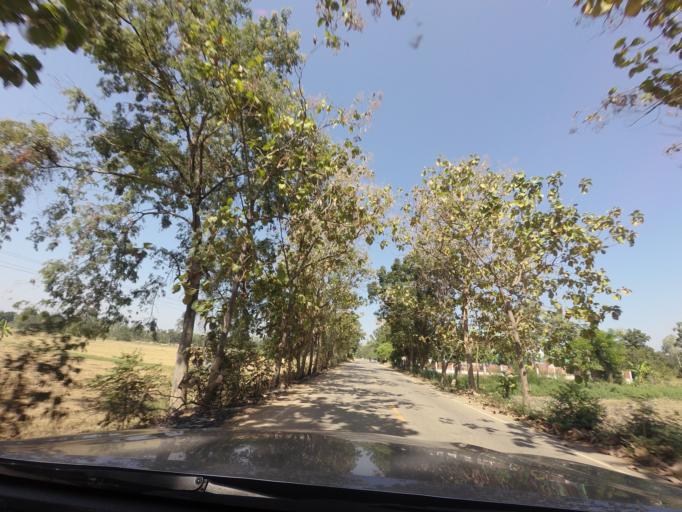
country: TH
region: Sukhothai
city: Si Samrong
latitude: 17.1425
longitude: 99.7704
